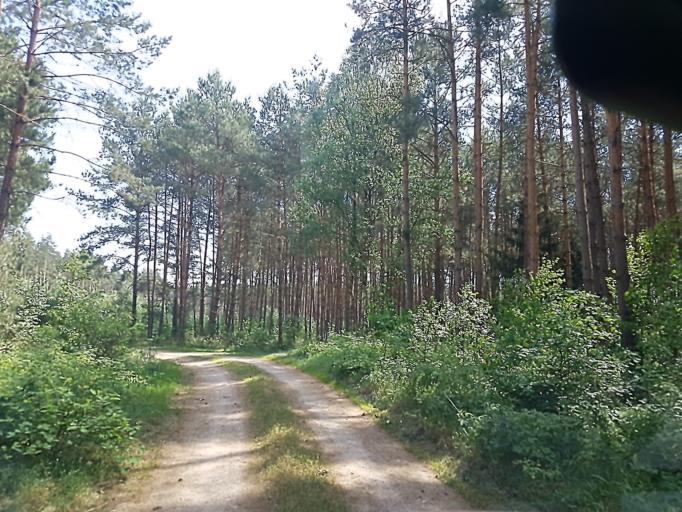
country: DE
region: Brandenburg
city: Gorzke
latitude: 52.0936
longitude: 12.3210
